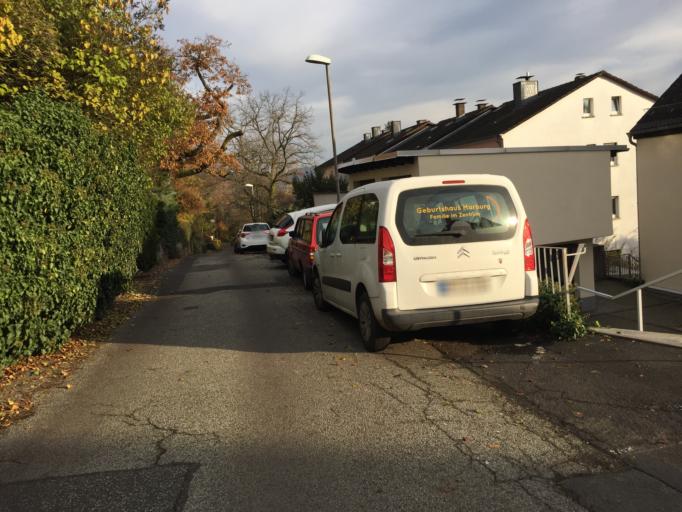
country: DE
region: Hesse
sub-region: Regierungsbezirk Giessen
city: Marburg an der Lahn
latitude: 50.8072
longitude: 8.7576
